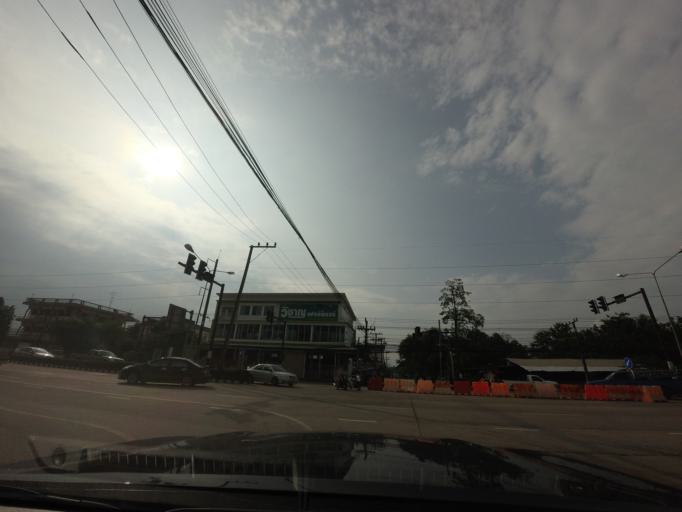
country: TH
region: Nong Khai
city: Nong Khai
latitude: 17.8786
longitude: 102.7467
